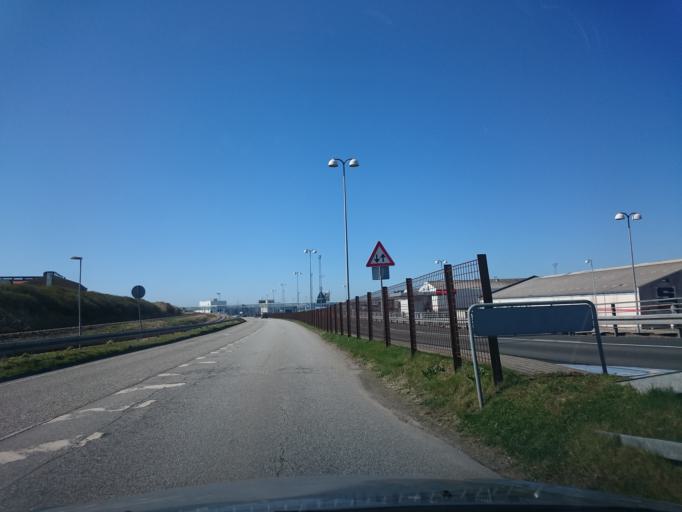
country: DK
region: North Denmark
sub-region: Hjorring Kommune
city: Hirtshals
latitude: 57.5898
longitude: 9.9721
